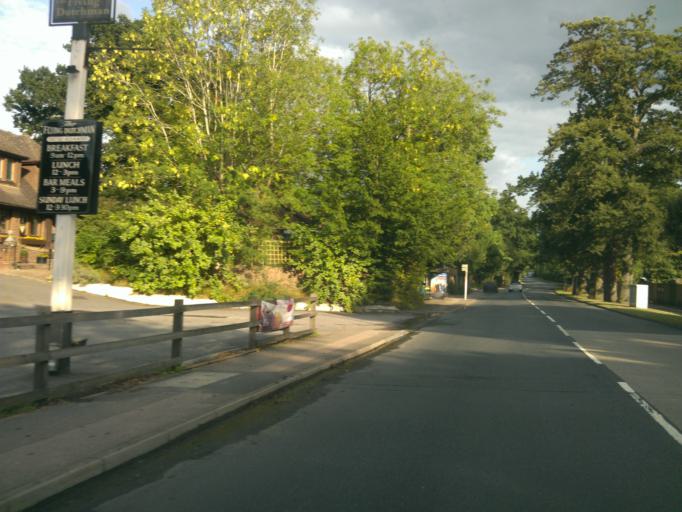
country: GB
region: England
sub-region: Kent
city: Tonbridge
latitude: 51.2131
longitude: 0.2495
